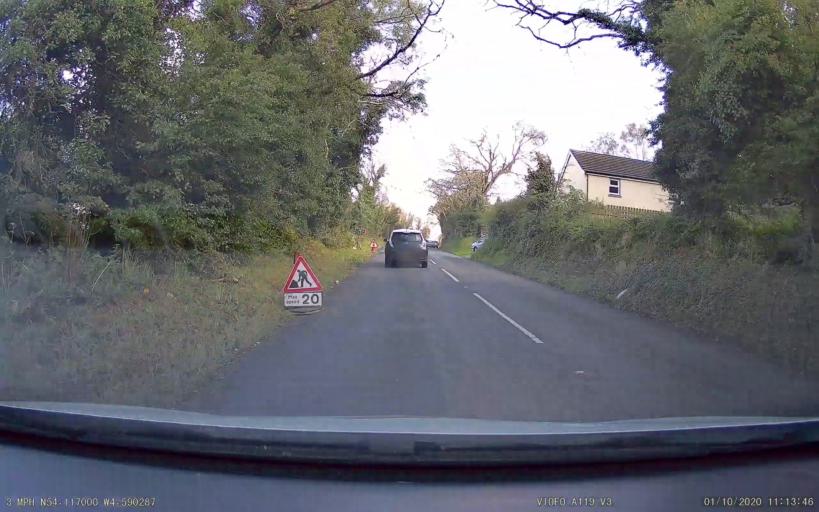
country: IM
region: Castletown
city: Castletown
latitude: 54.1170
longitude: -4.5903
